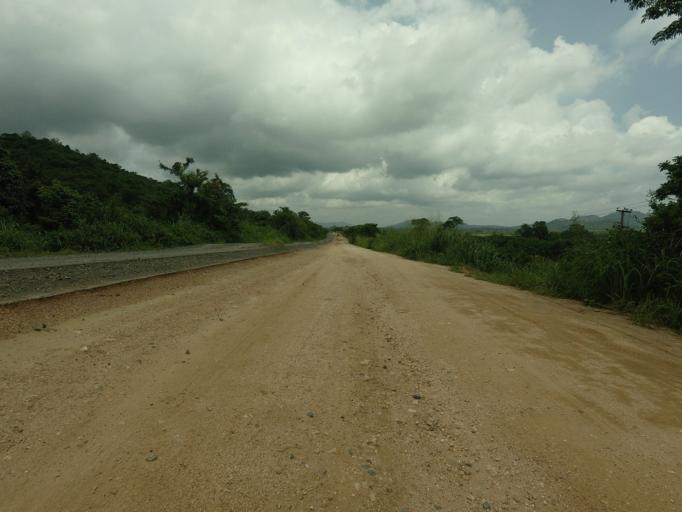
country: GH
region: Volta
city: Ho
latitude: 6.6596
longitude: 0.3046
